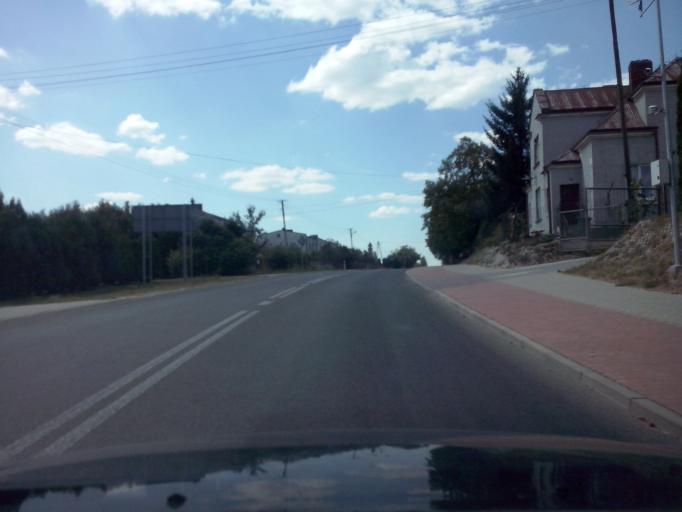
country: PL
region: Swietokrzyskie
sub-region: Powiat staszowski
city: Szydlow
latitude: 50.5886
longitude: 20.9980
